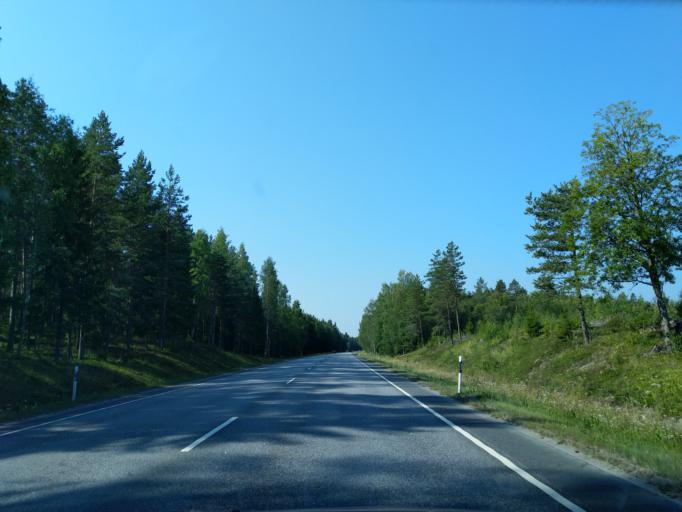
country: FI
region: Satakunta
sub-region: Pori
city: Noormarkku
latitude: 61.6347
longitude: 21.9371
